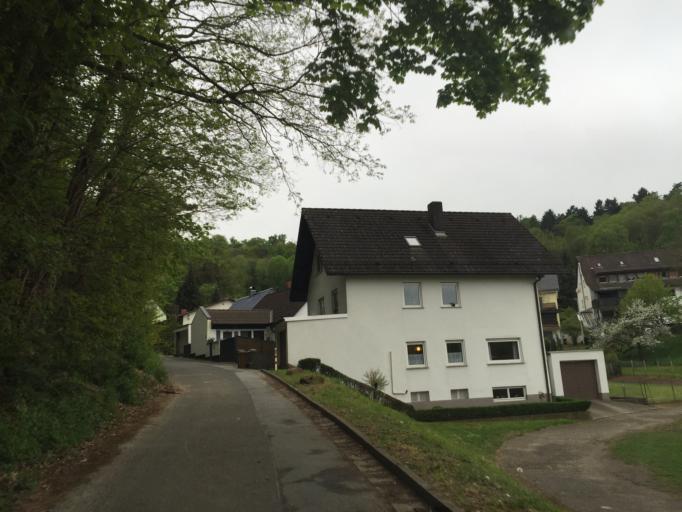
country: DE
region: Baden-Wuerttemberg
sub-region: Karlsruhe Region
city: Weinheim
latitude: 49.5277
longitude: 8.6749
